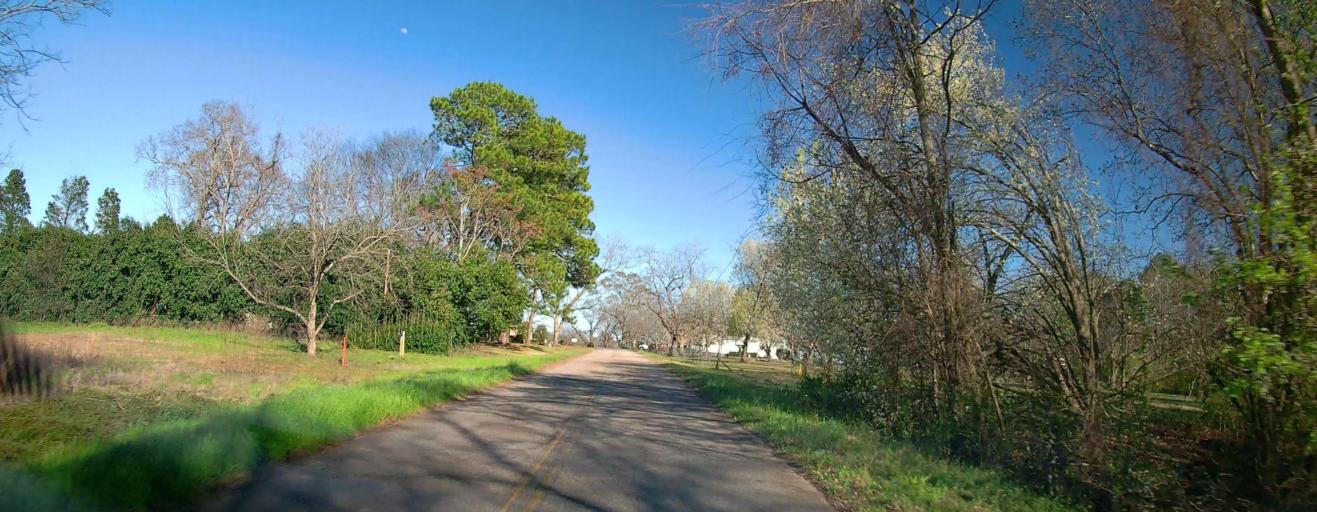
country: US
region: Georgia
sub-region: Peach County
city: Fort Valley
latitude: 32.6378
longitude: -83.8625
